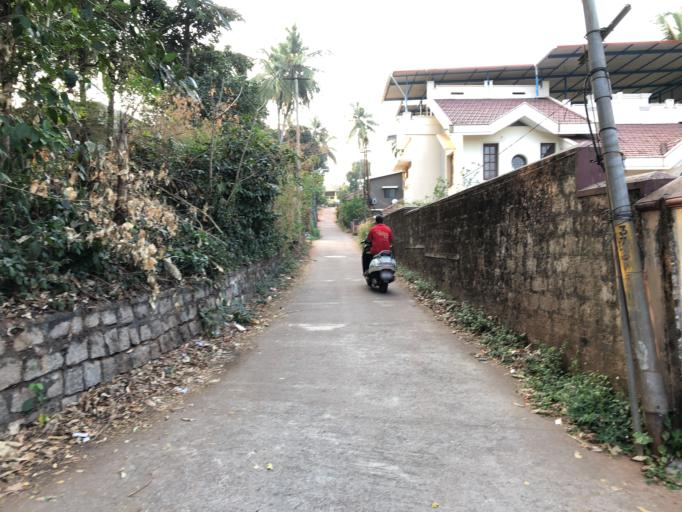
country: IN
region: Karnataka
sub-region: Dakshina Kannada
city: Mangalore
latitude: 12.8869
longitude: 74.8672
